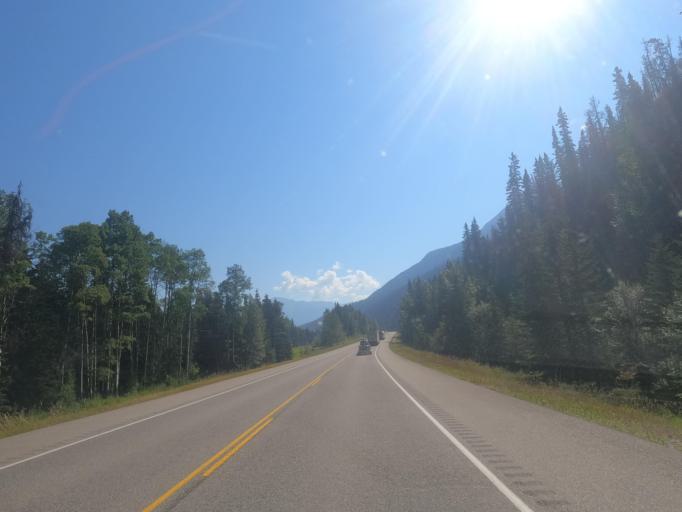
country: CA
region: Alberta
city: Jasper Park Lodge
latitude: 52.8598
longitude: -118.1751
